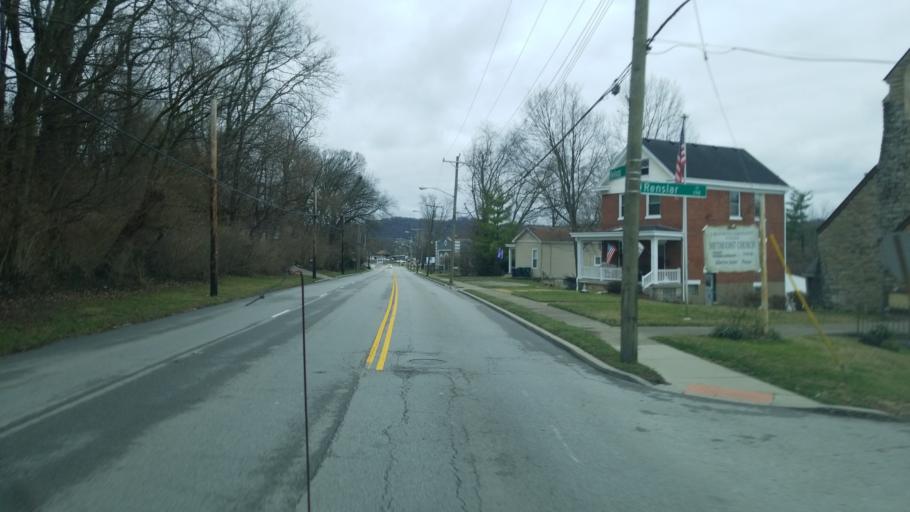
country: US
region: Kentucky
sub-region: Campbell County
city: Fort Thomas
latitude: 39.0694
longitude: -84.4240
